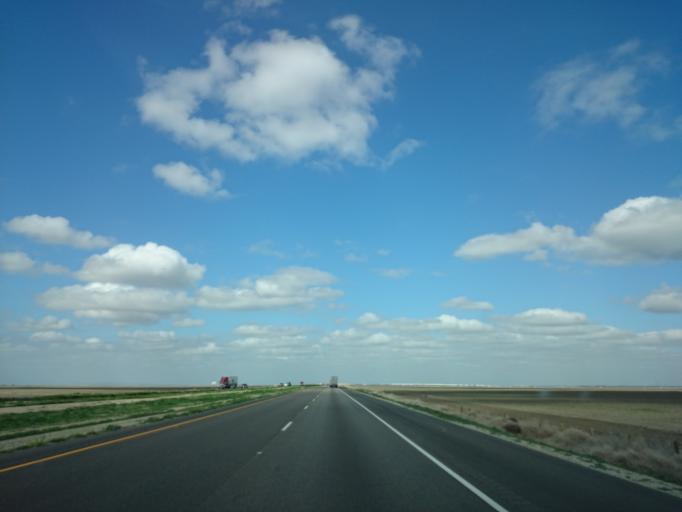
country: US
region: California
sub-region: Kern County
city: Greenfield
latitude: 35.1323
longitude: -119.0781
